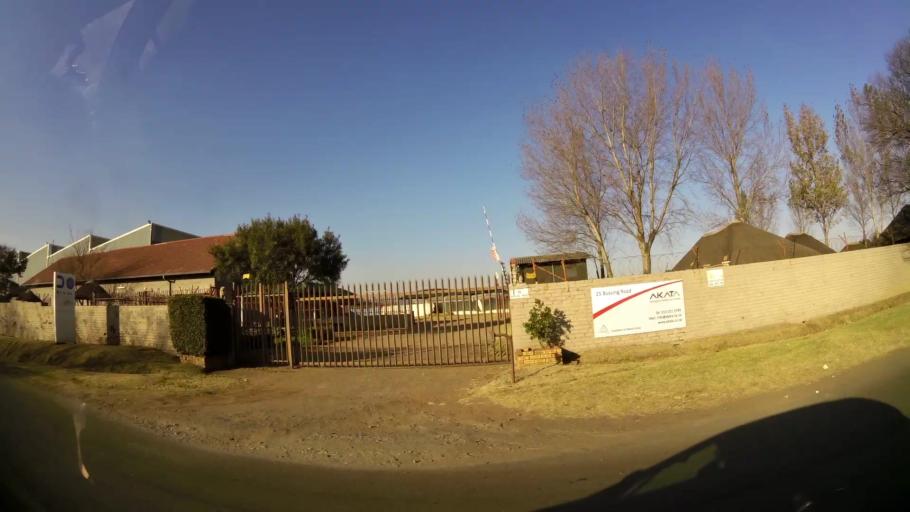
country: ZA
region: Gauteng
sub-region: West Rand District Municipality
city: Randfontein
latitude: -26.2011
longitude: 27.6836
